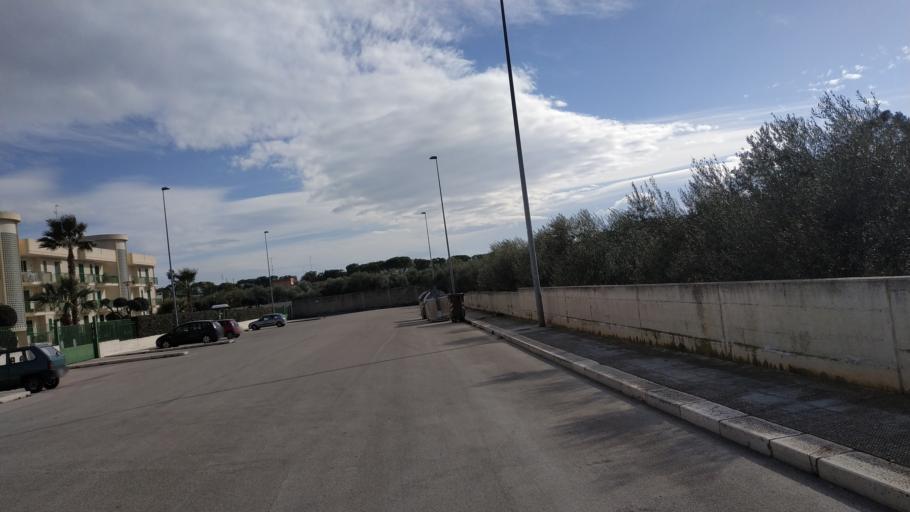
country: IT
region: Apulia
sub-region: Provincia di Bari
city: Bitonto
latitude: 41.1092
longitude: 16.6768
